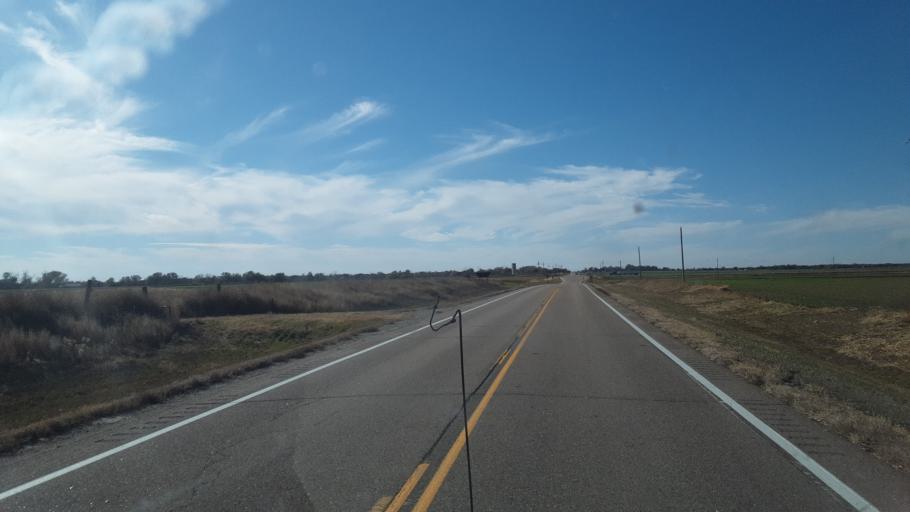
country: US
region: Kansas
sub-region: Pawnee County
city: Larned
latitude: 38.1895
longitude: -99.3086
